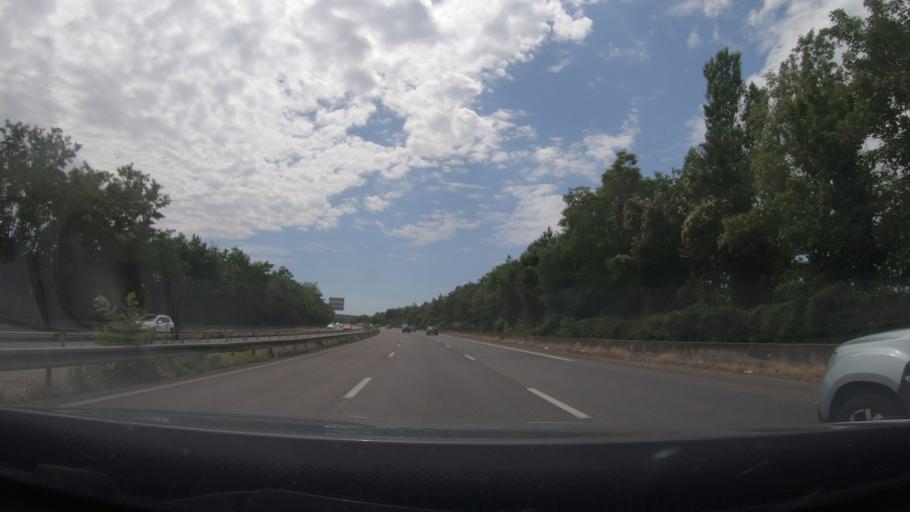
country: FR
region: Lorraine
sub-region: Departement de la Moselle
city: Moulins-les-Metz
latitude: 49.0905
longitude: 6.1078
